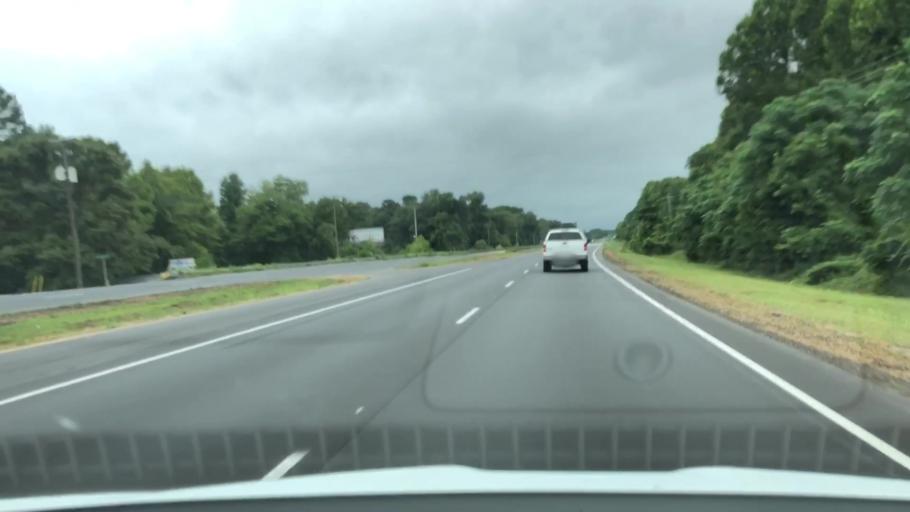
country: US
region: North Carolina
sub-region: Lenoir County
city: Kinston
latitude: 35.2603
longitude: -77.6167
